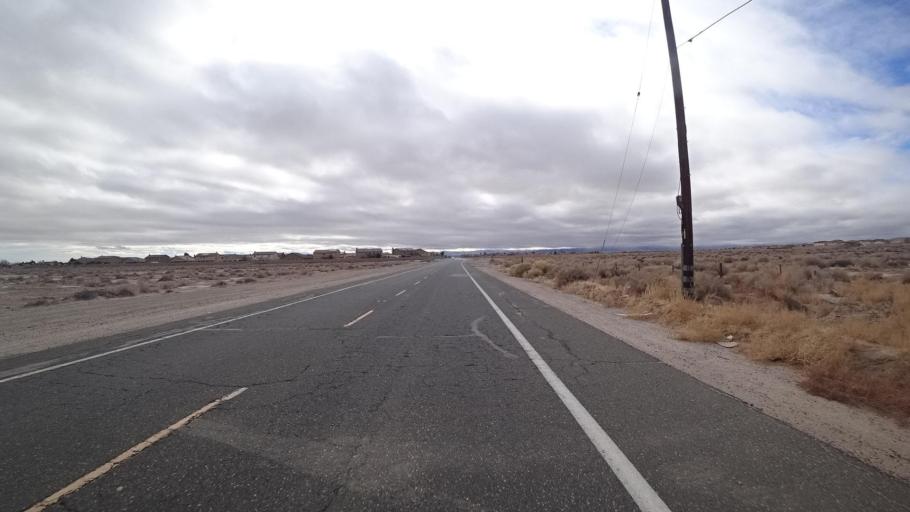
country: US
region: California
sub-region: Kern County
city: Rosamond
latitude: 34.8588
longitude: -118.1760
